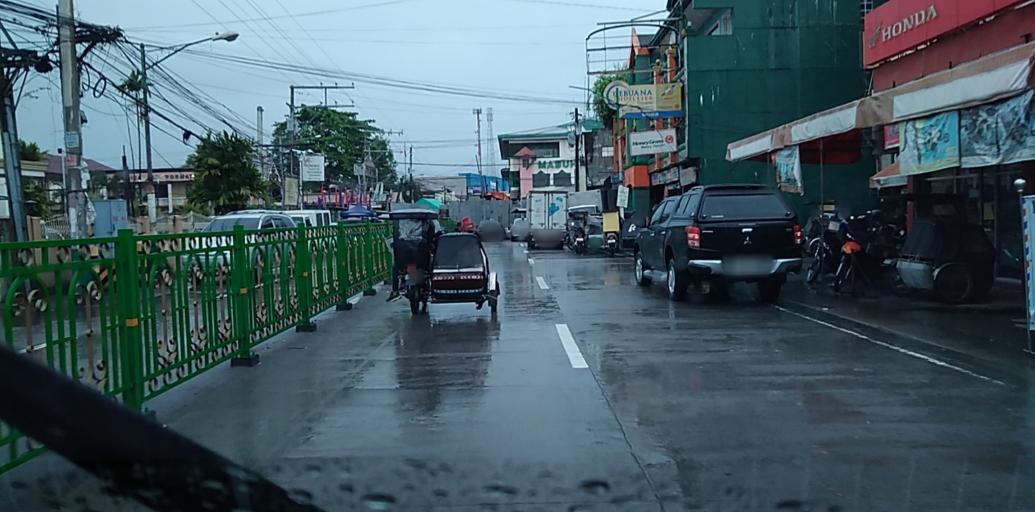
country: PH
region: Central Luzon
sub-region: Province of Pampanga
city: Mexico
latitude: 15.0637
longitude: 120.7204
